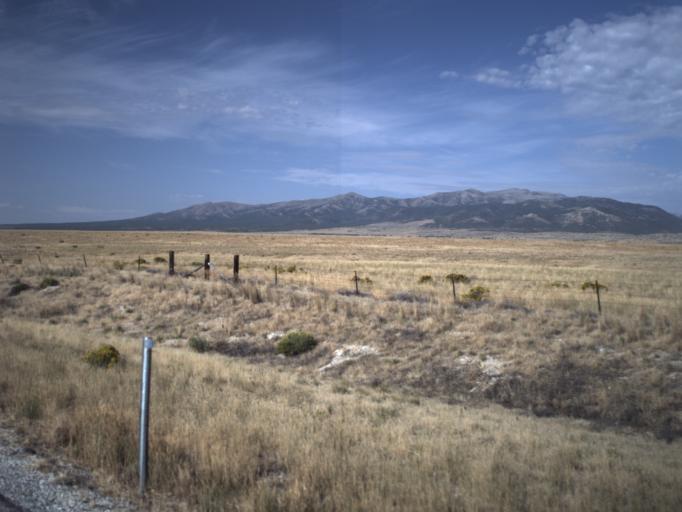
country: US
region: Idaho
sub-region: Oneida County
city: Malad City
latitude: 41.9483
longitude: -113.0797
